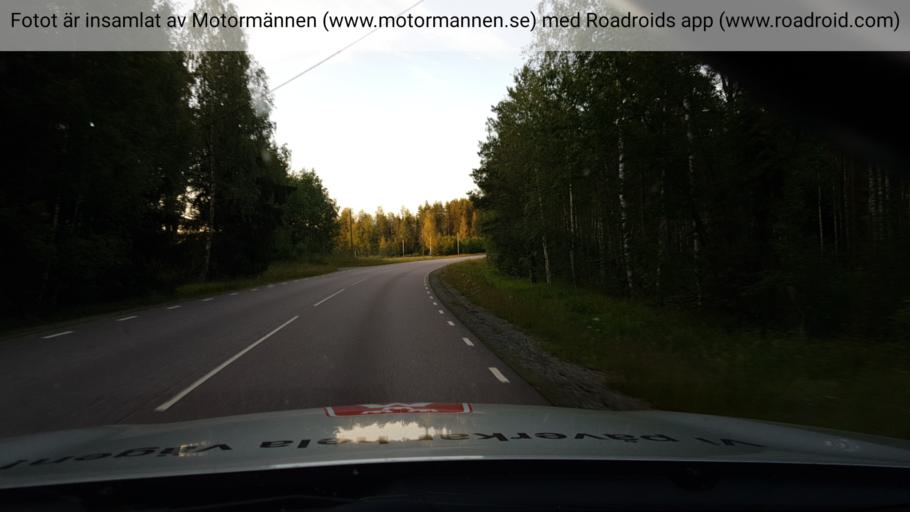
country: SE
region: Vaestmanland
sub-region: Surahammars Kommun
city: Ramnas
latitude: 59.8791
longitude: 16.0470
